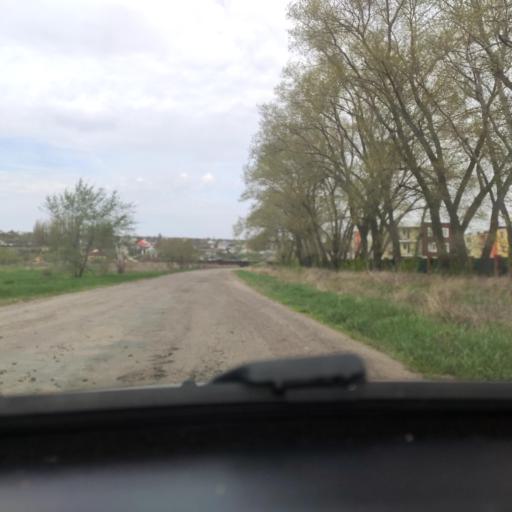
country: RU
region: Voronezj
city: Pridonskoy
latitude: 51.7281
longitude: 39.0596
